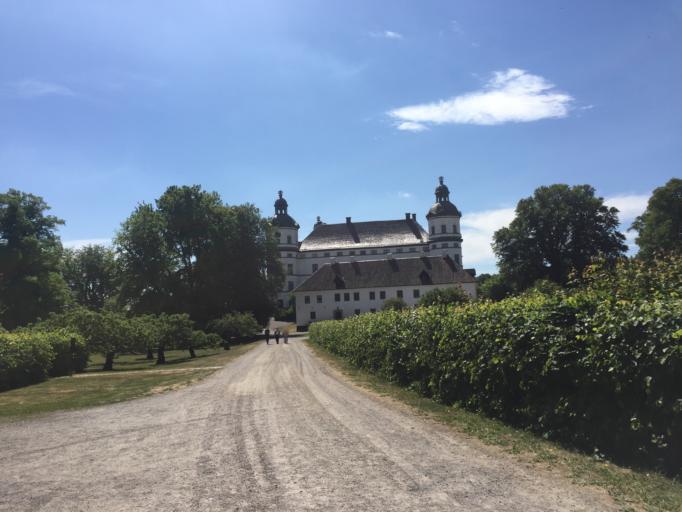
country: SE
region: Stockholm
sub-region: Sigtuna Kommun
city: Sigtuna
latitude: 59.7048
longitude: 17.6225
